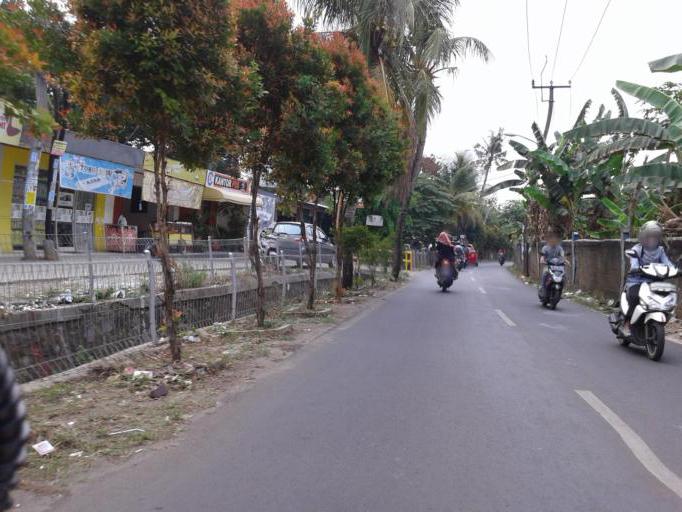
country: ID
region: West Java
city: Pamulang
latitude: -6.3202
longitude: 106.7616
